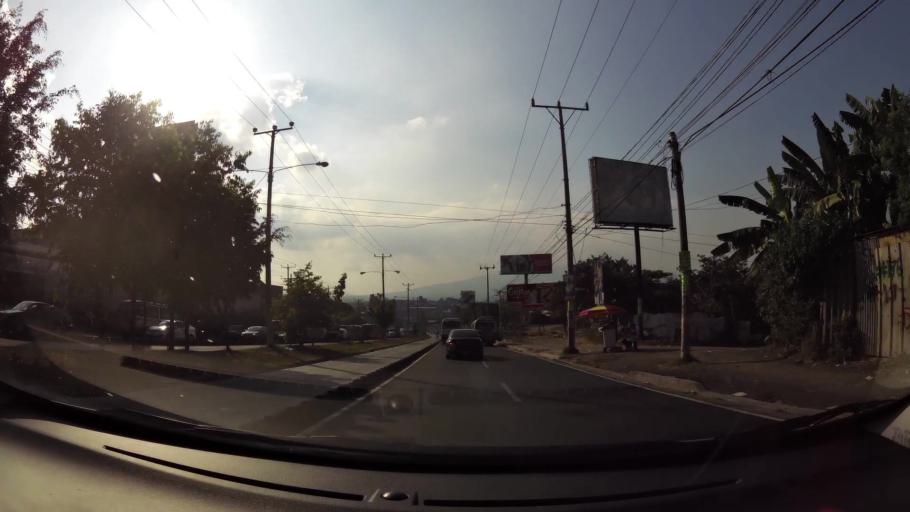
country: SV
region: San Salvador
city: Soyapango
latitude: 13.7013
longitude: -89.1579
